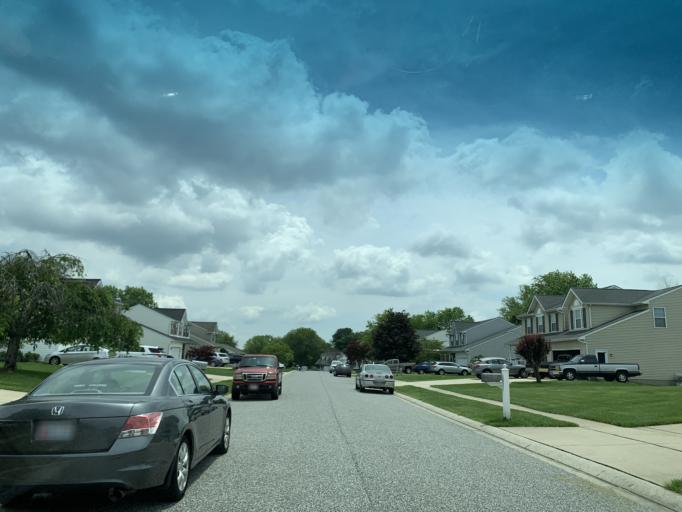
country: US
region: Maryland
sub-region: Harford County
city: South Bel Air
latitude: 39.5422
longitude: -76.3035
